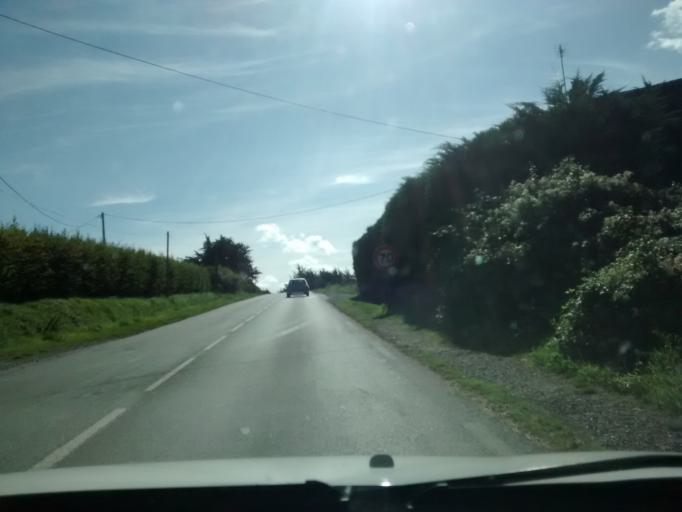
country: FR
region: Brittany
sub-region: Departement d'Ille-et-Vilaine
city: Saint-Briac-sur-Mer
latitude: 48.6154
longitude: -2.1366
